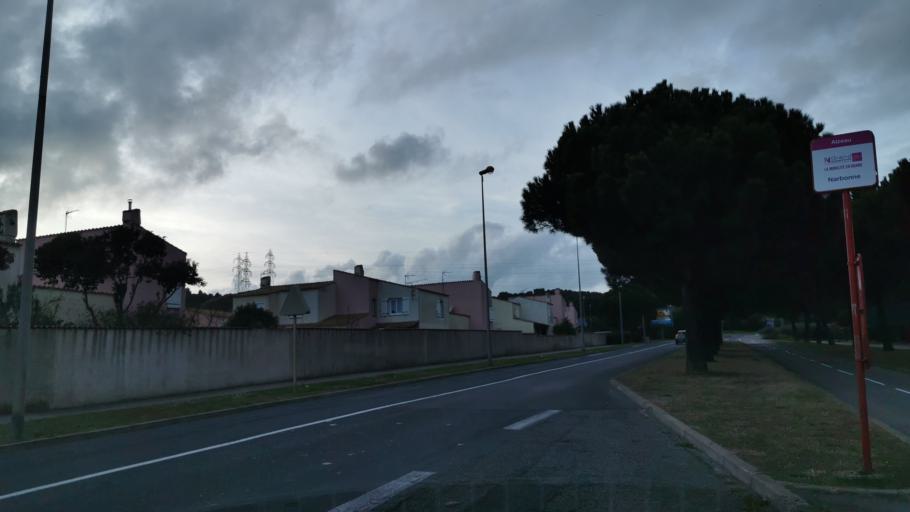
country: FR
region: Languedoc-Roussillon
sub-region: Departement de l'Aude
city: Narbonne
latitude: 43.1856
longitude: 2.9742
